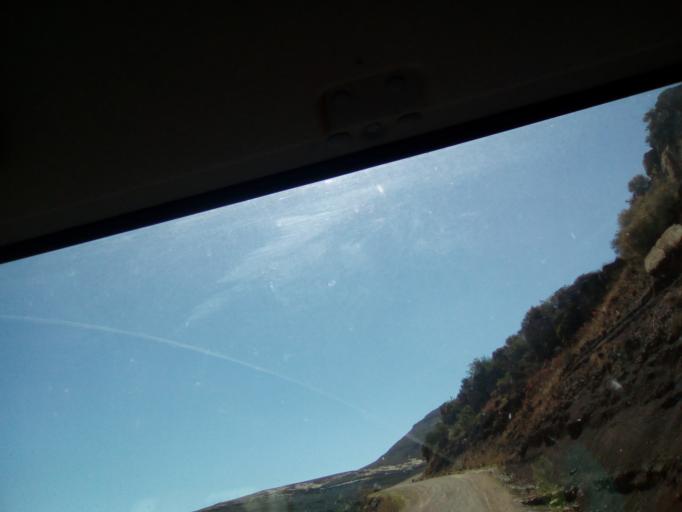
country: LS
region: Qacha's Nek
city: Qacha's Nek
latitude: -30.0432
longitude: 28.6509
